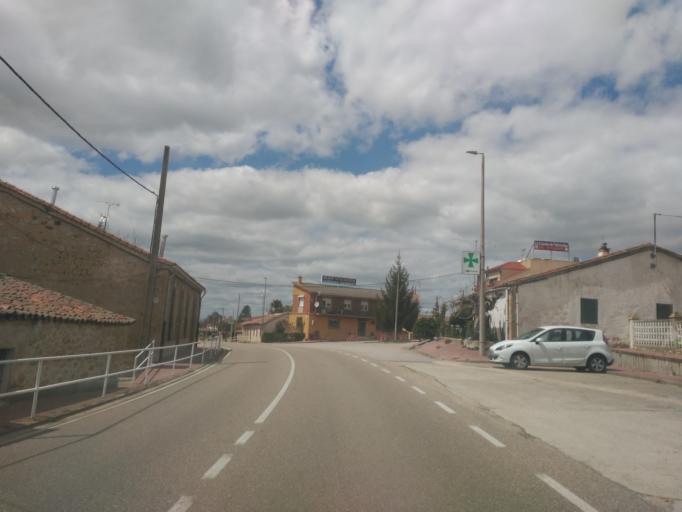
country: ES
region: Castille and Leon
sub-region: Provincia de Salamanca
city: Valverdon
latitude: 41.0472
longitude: -5.7684
